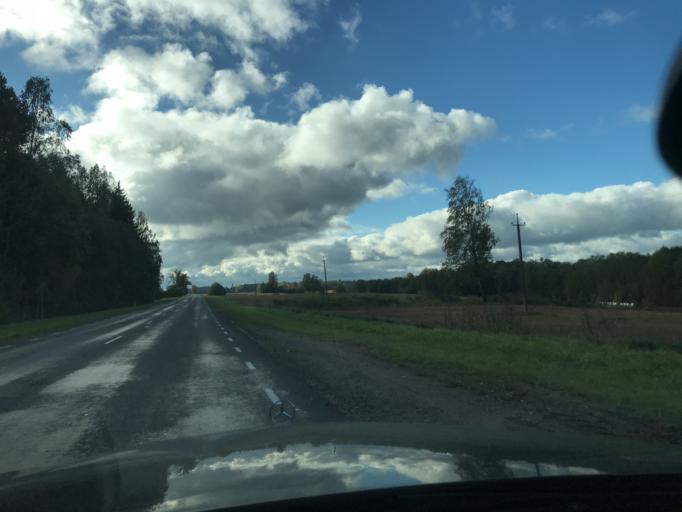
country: EE
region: Tartu
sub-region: Elva linn
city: Elva
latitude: 57.9815
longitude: 26.2613
